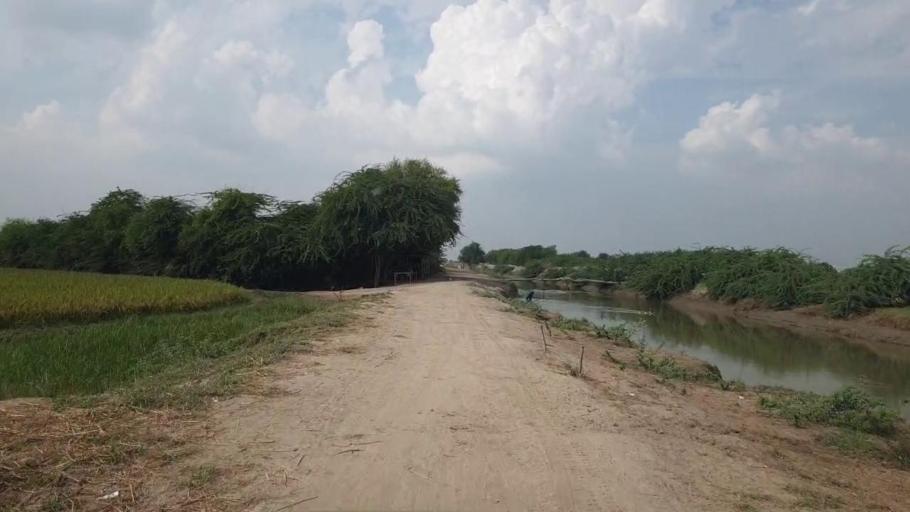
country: PK
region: Sindh
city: Badin
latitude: 24.5647
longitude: 68.6371
